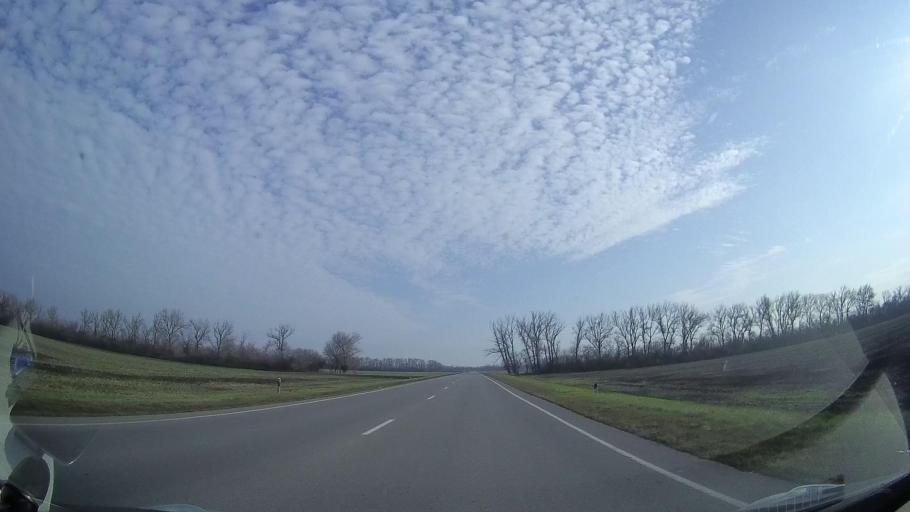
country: RU
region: Rostov
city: Tselina
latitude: 46.5226
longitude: 41.1335
